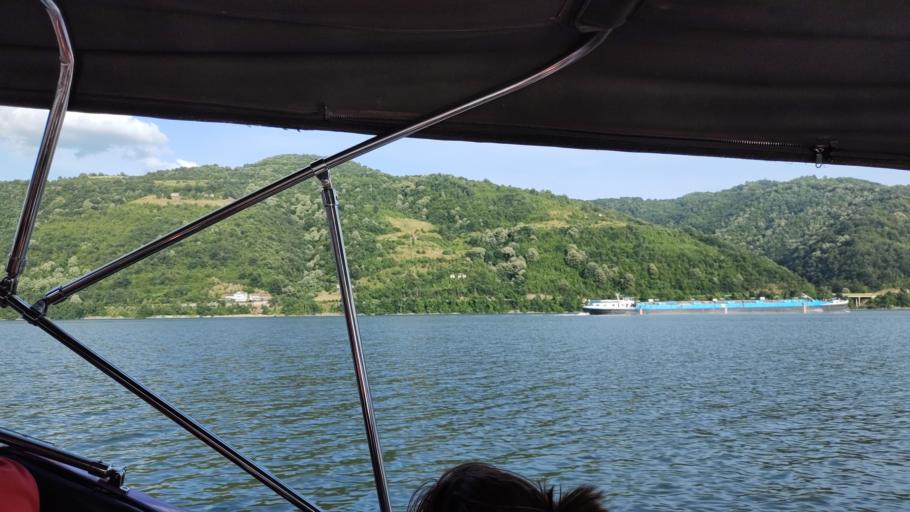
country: RO
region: Mehedinti
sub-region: Comuna Svinita
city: Svinita
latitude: 44.5224
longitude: 22.2064
